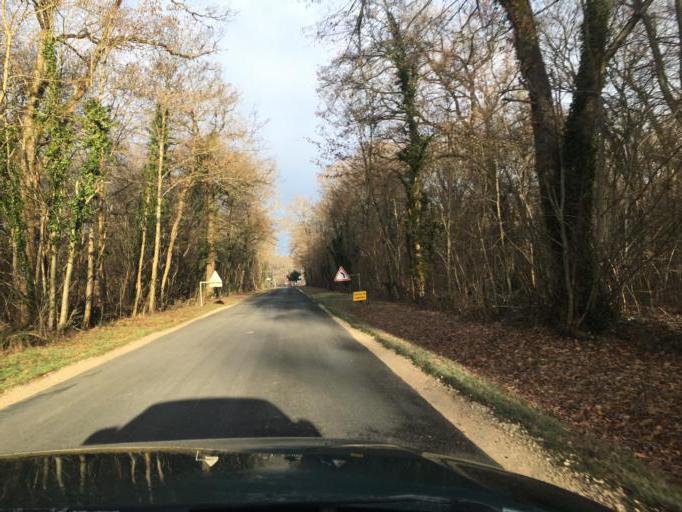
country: FR
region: Centre
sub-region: Departement du Loiret
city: Mareau-aux-Pres
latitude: 47.8166
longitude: 1.8078
